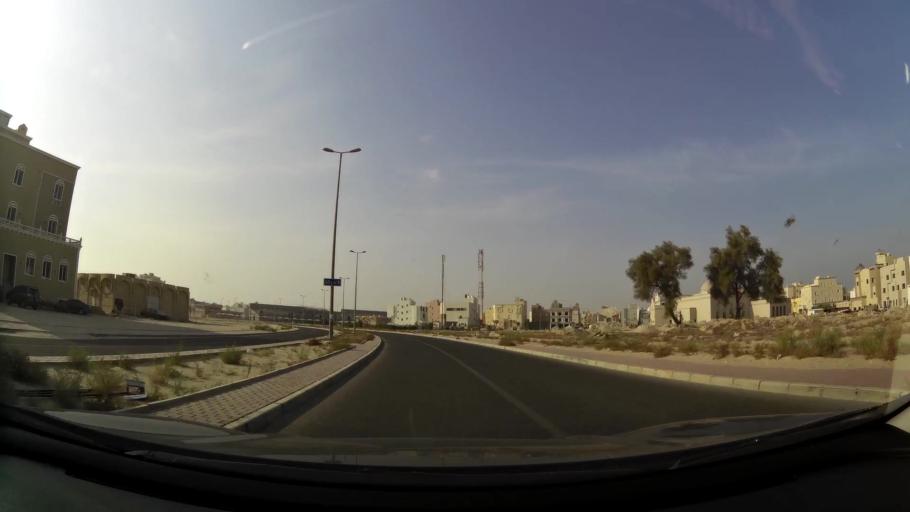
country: KW
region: Mubarak al Kabir
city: Mubarak al Kabir
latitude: 29.1936
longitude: 48.1051
